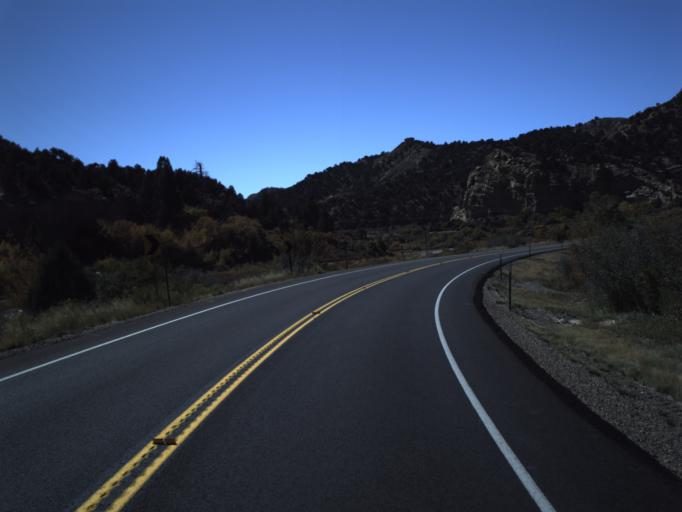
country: US
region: Utah
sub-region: Garfield County
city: Panguitch
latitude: 37.6042
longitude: -111.9105
